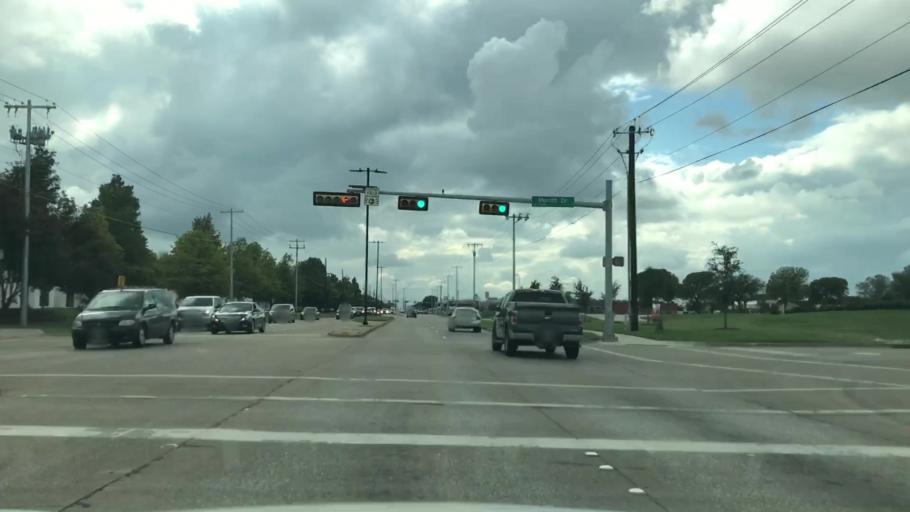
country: US
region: Texas
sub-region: Dallas County
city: Garland
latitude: 32.8945
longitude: -96.6785
